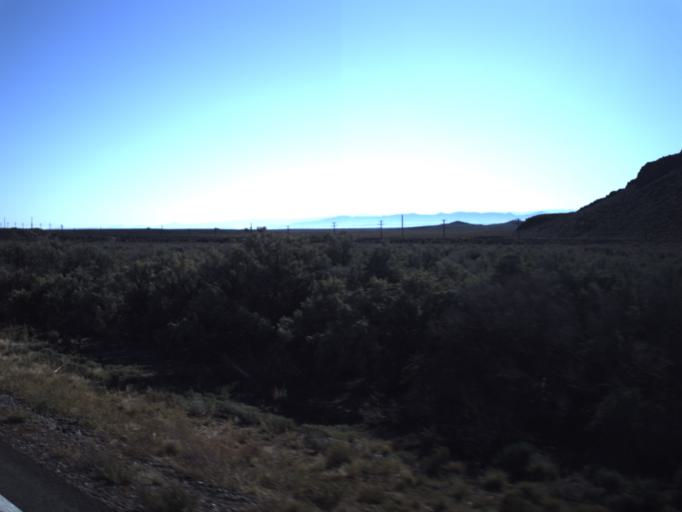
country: US
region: Utah
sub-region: Washington County
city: Enterprise
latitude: 37.7890
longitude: -113.9529
